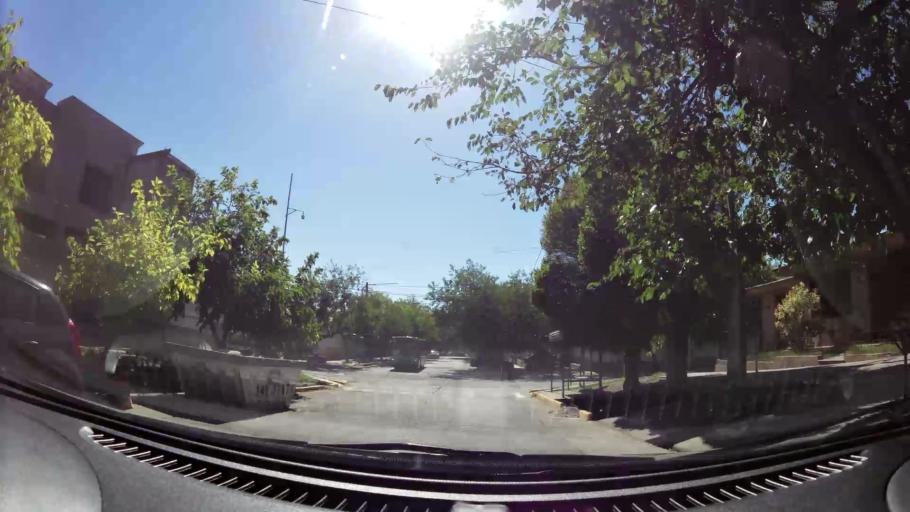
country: AR
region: Mendoza
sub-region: Departamento de Godoy Cruz
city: Godoy Cruz
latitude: -32.9174
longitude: -68.8744
